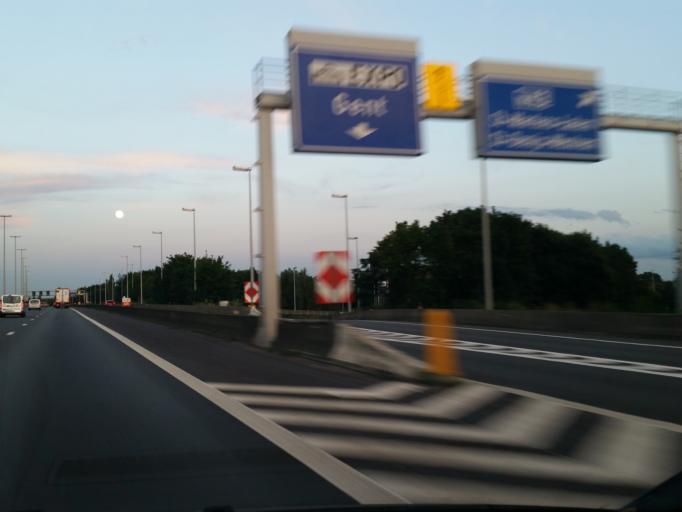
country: BE
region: Flanders
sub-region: Provincie Oost-Vlaanderen
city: Sint-Martens-Latem
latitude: 51.0218
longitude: 3.6816
